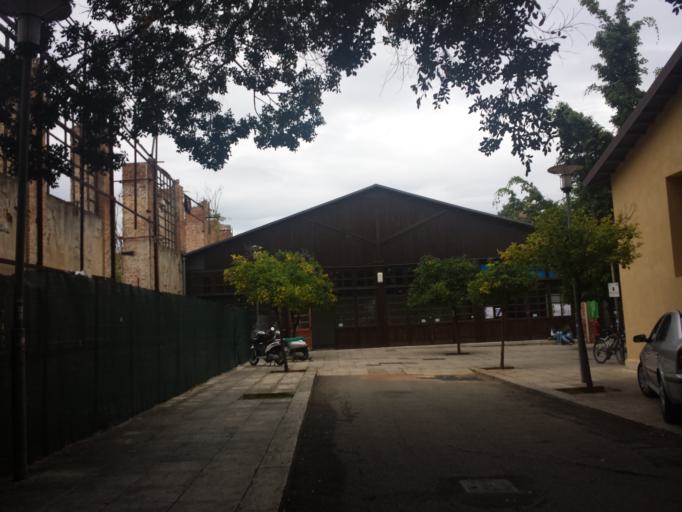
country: IT
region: Sicily
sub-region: Palermo
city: Palermo
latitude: 38.1185
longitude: 13.3384
